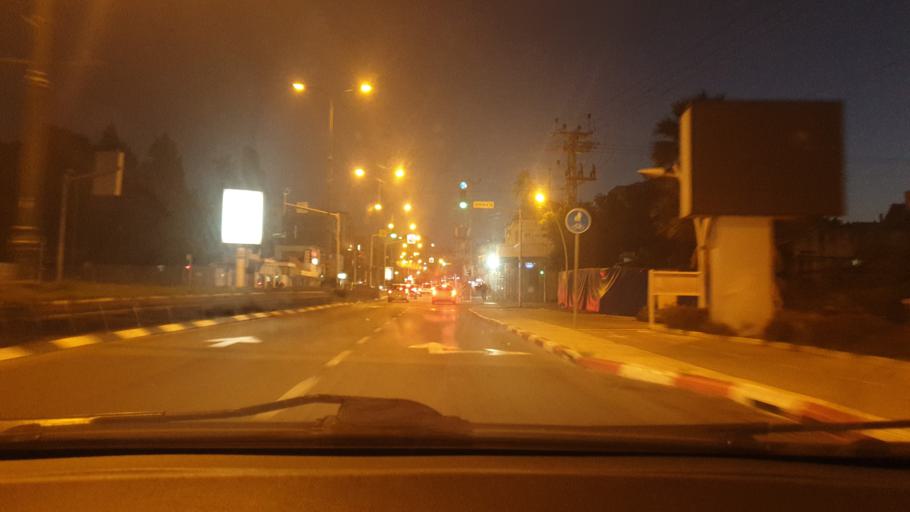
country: IL
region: Central District
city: Rishon LeZiyyon
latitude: 31.9739
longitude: 34.8069
